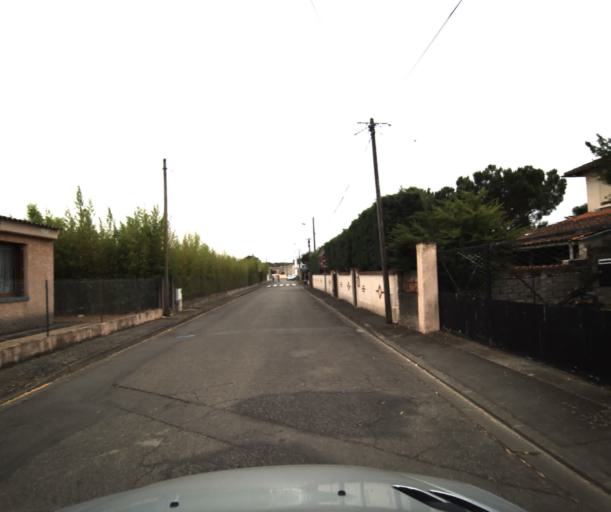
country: FR
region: Midi-Pyrenees
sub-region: Departement de la Haute-Garonne
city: Portet-sur-Garonne
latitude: 43.5440
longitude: 1.4087
